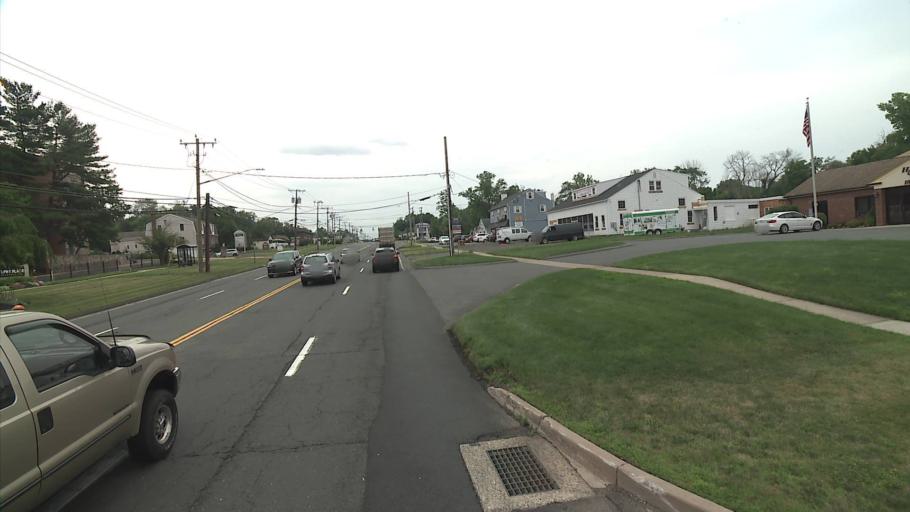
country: US
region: Connecticut
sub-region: Hartford County
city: Wethersfield
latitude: 41.6769
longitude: -72.6506
